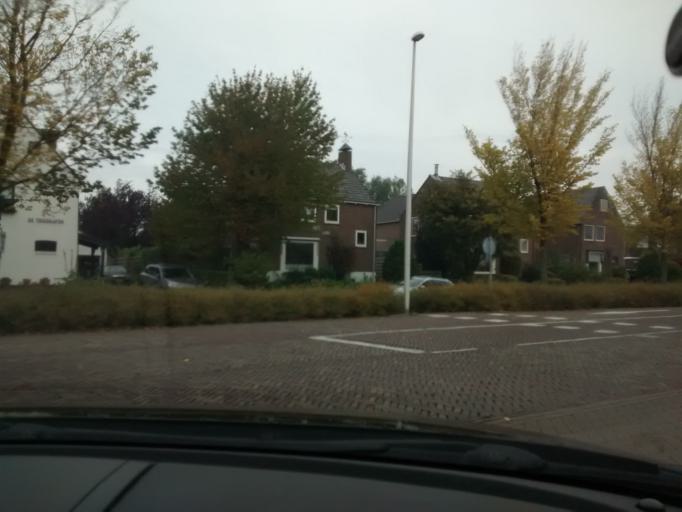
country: NL
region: South Holland
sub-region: Gemeente Hellevoetsluis
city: Hellevoetsluis
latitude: 51.8238
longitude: 4.1337
